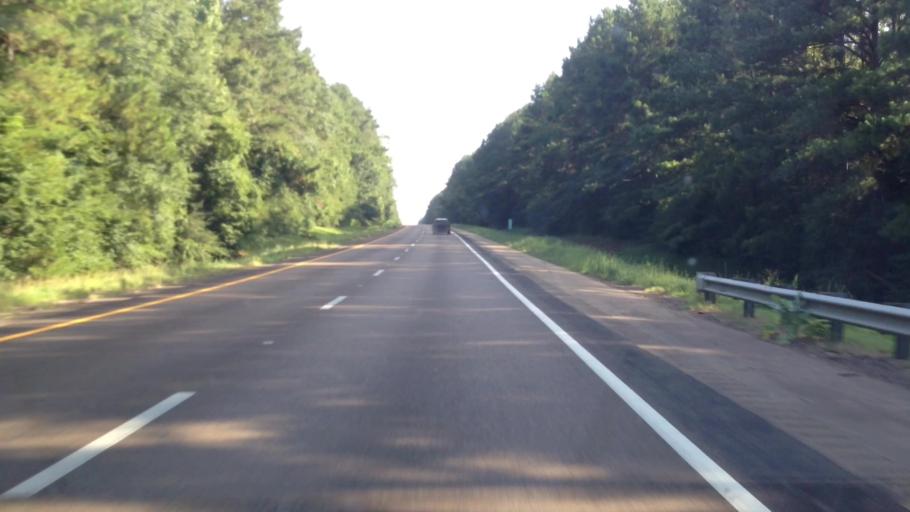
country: US
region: Mississippi
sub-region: Pike County
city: Summit
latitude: 31.3318
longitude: -90.4770
